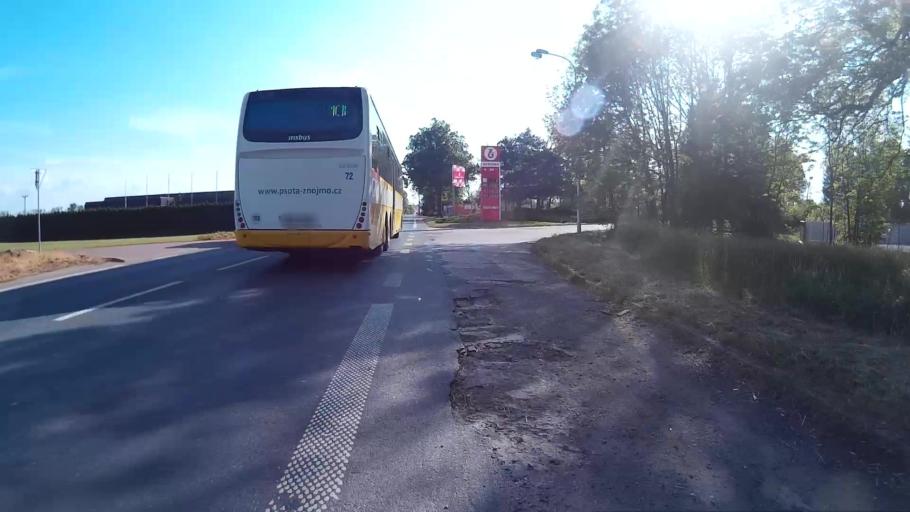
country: CZ
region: South Moravian
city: Pohorelice
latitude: 48.9886
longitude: 16.5368
